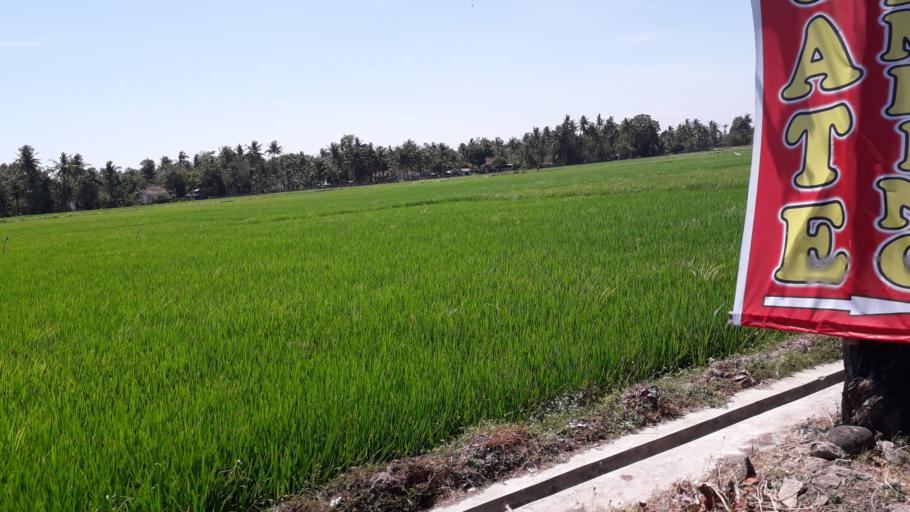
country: ID
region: Daerah Istimewa Yogyakarta
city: Pundong
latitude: -7.9758
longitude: 110.3180
